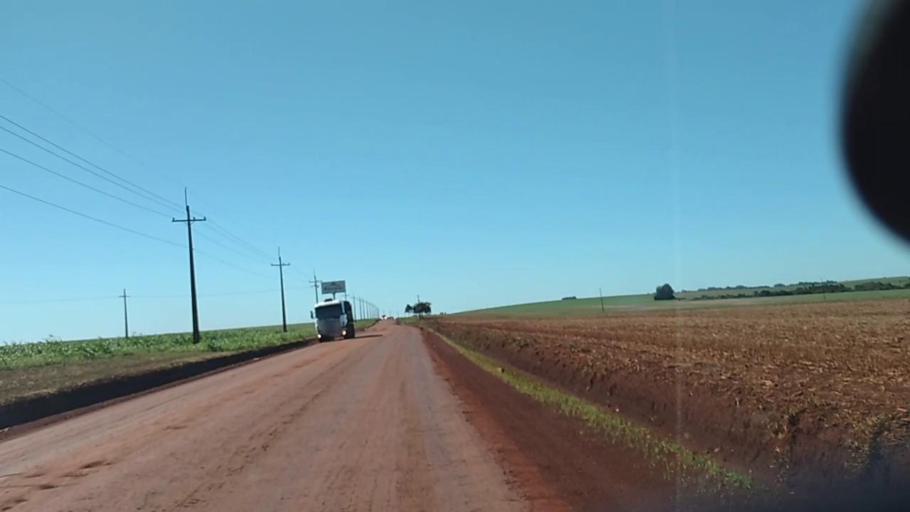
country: PY
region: Alto Parana
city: Naranjal
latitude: -25.9403
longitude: -55.2963
